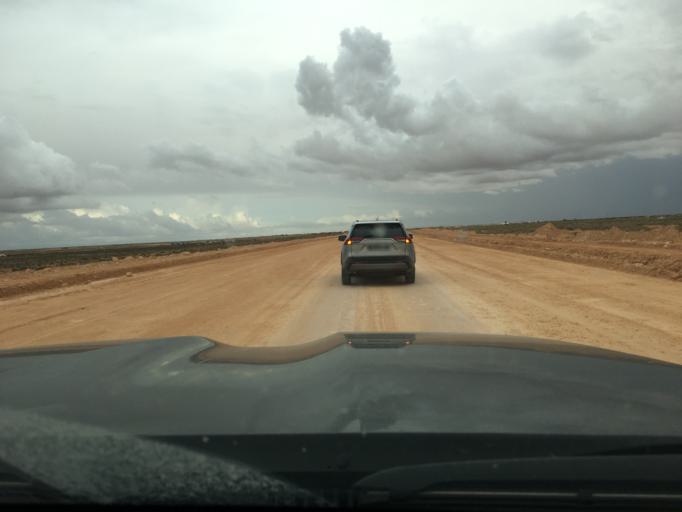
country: TN
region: Madanin
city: Medenine
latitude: 33.2812
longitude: 10.5952
